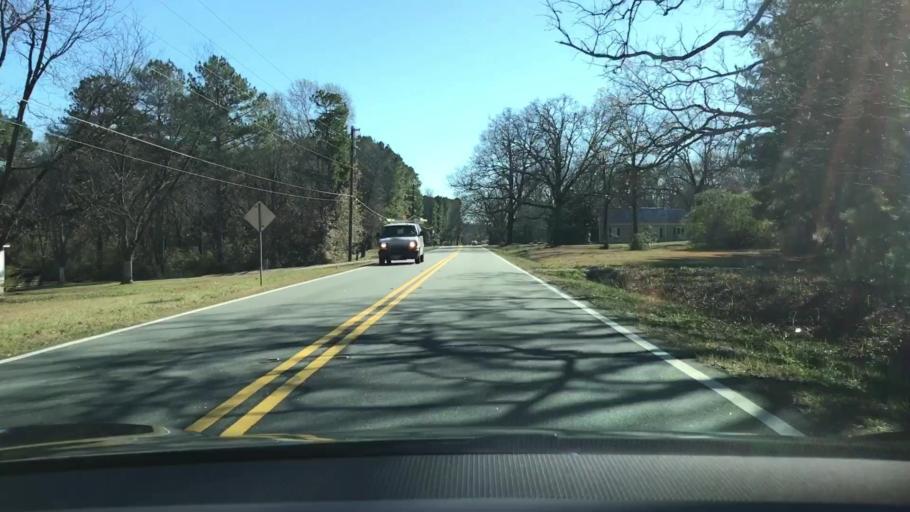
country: US
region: Georgia
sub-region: Walton County
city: Monroe
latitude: 33.8713
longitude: -83.7574
